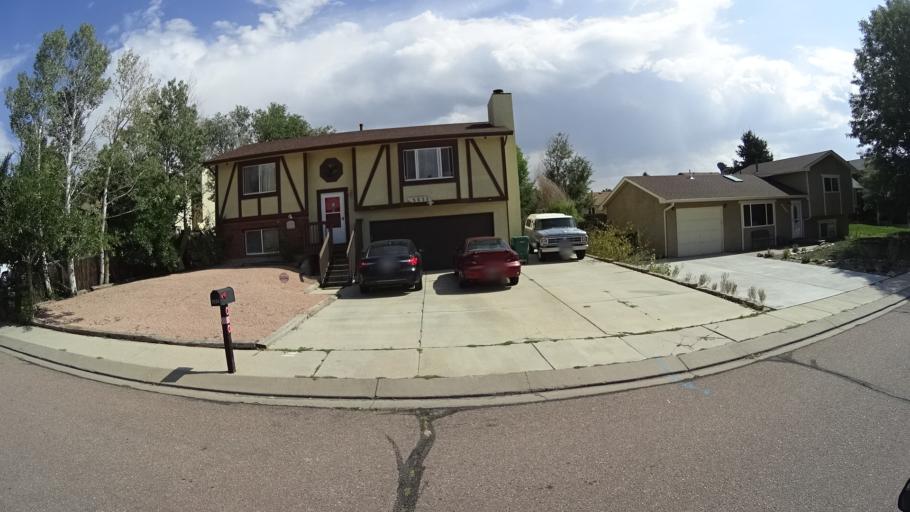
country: US
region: Colorado
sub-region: El Paso County
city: Cimarron Hills
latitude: 38.8644
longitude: -104.7250
